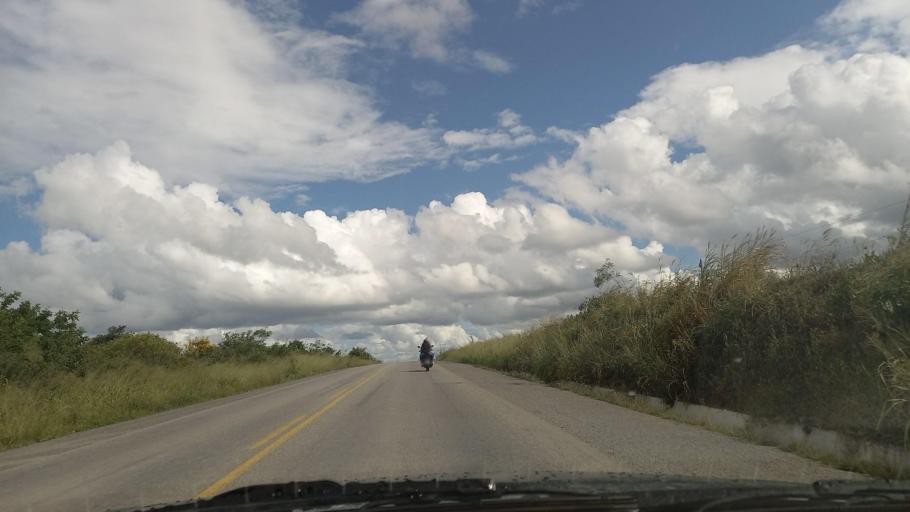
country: BR
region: Pernambuco
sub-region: Lajedo
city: Lajedo
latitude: -8.5885
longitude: -36.2896
